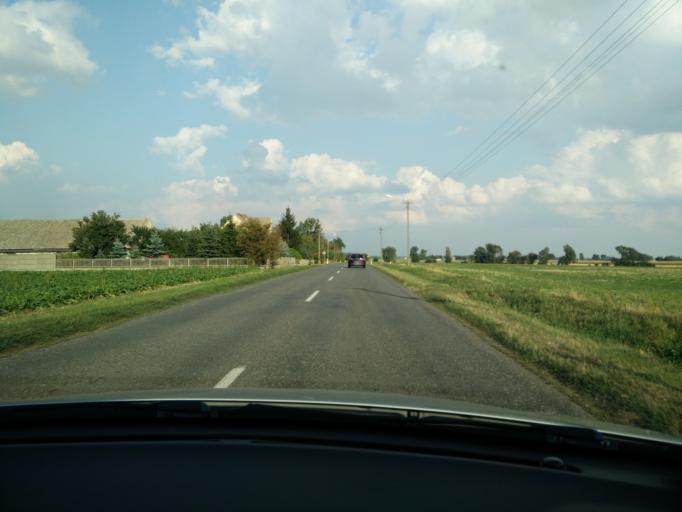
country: PL
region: Greater Poland Voivodeship
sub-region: Powiat sredzki
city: Dominowo
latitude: 52.2383
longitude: 17.3421
